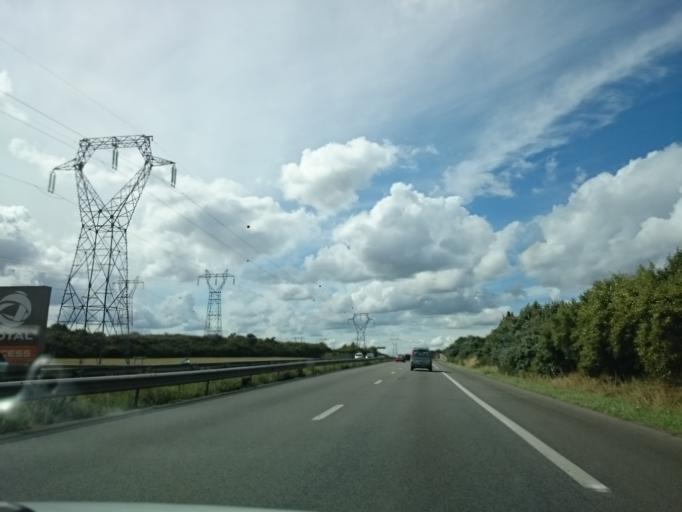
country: FR
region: Pays de la Loire
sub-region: Departement de la Loire-Atlantique
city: Reze
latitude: 47.1656
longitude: -1.5702
